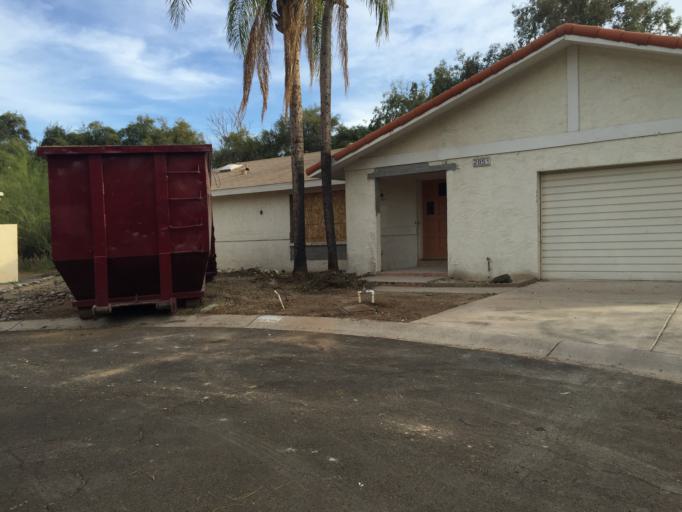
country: US
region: Arizona
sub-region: Maricopa County
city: Paradise Valley
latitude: 33.5705
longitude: -112.0186
